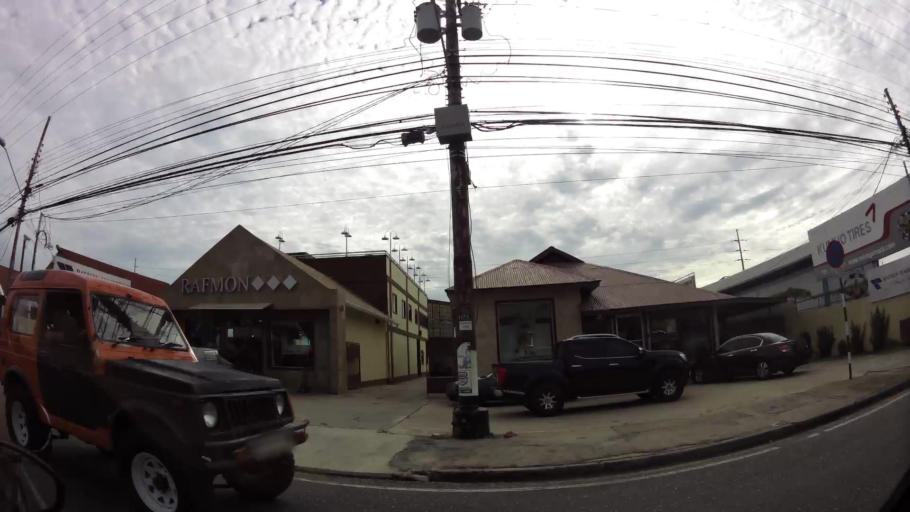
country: TT
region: City of Port of Spain
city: Mucurapo
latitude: 10.6714
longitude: -61.5387
